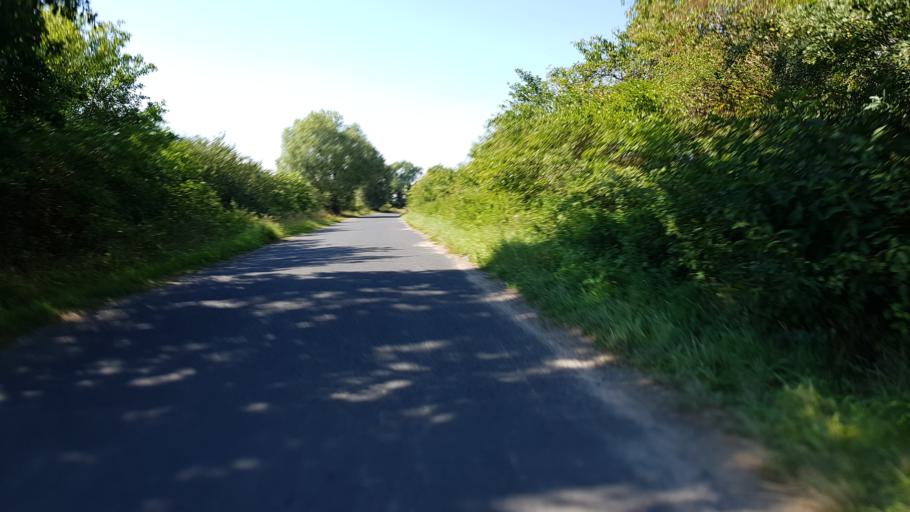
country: PL
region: West Pomeranian Voivodeship
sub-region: Powiat gryfinski
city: Gryfino
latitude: 53.1592
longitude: 14.4924
